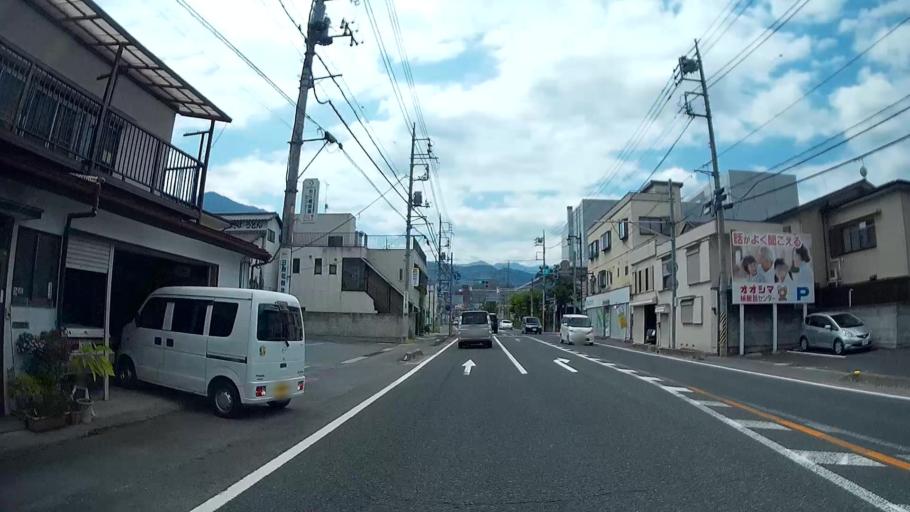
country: JP
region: Saitama
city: Chichibu
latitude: 35.9924
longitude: 139.0865
